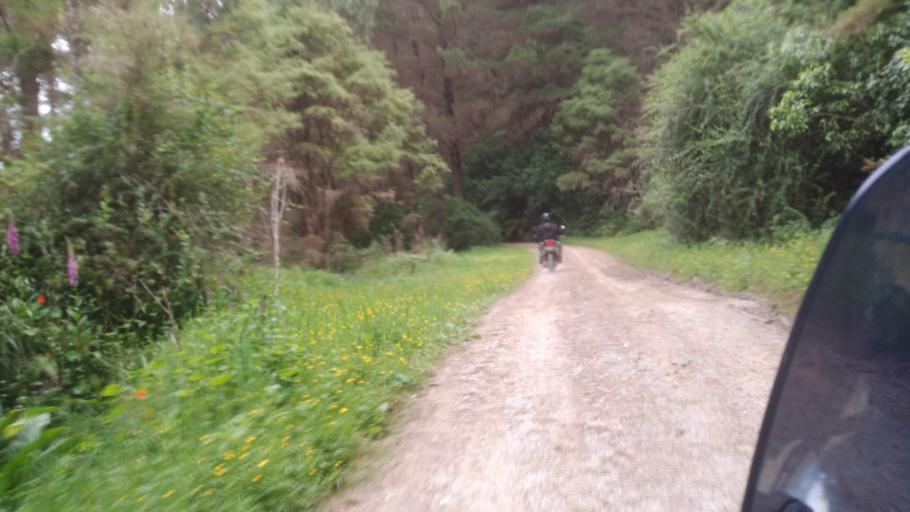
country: NZ
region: Gisborne
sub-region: Gisborne District
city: Gisborne
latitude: -38.4577
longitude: 177.9108
